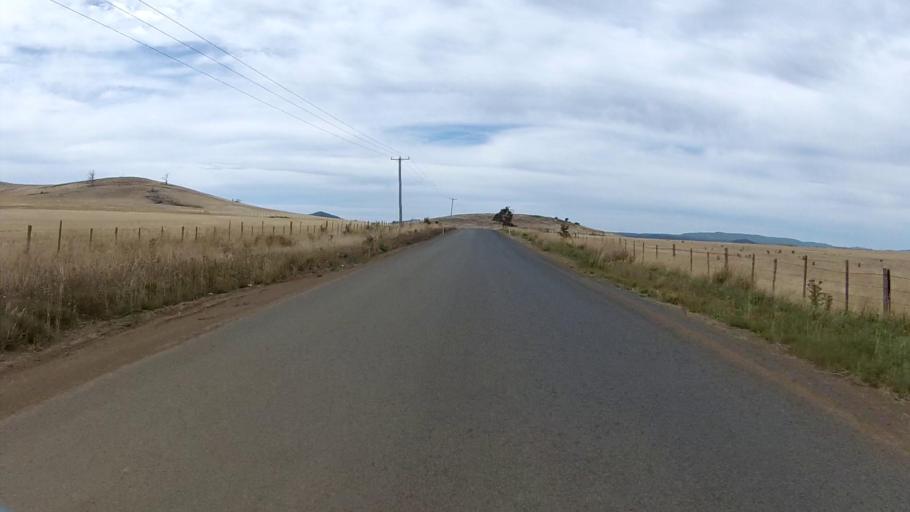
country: AU
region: Tasmania
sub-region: Sorell
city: Sorell
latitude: -42.8975
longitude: 147.7551
